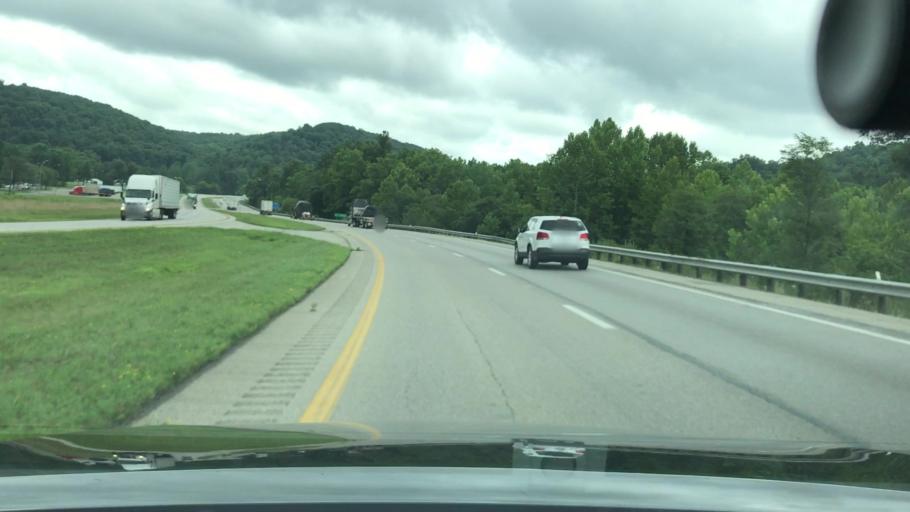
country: US
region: Ohio
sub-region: Jackson County
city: Jackson
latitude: 39.1671
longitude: -82.7422
